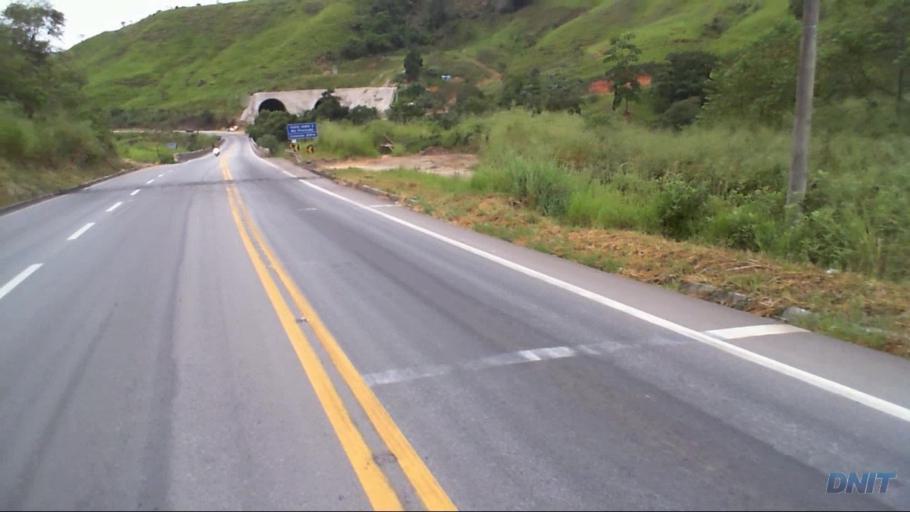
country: BR
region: Minas Gerais
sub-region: Timoteo
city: Timoteo
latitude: -19.6180
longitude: -42.7971
